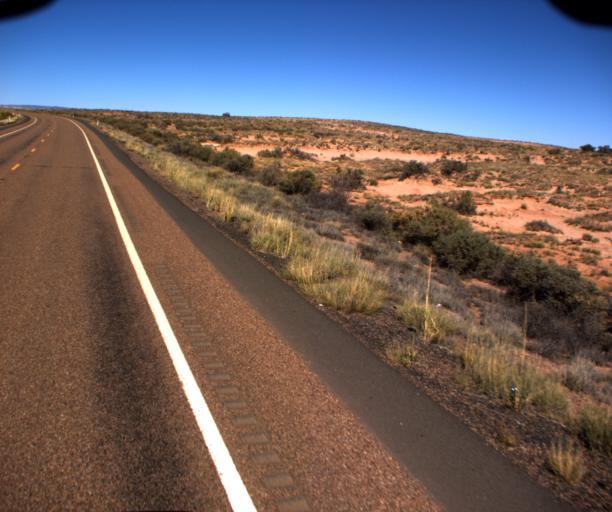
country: US
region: Arizona
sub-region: Navajo County
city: Holbrook
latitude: 35.0578
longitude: -110.0962
